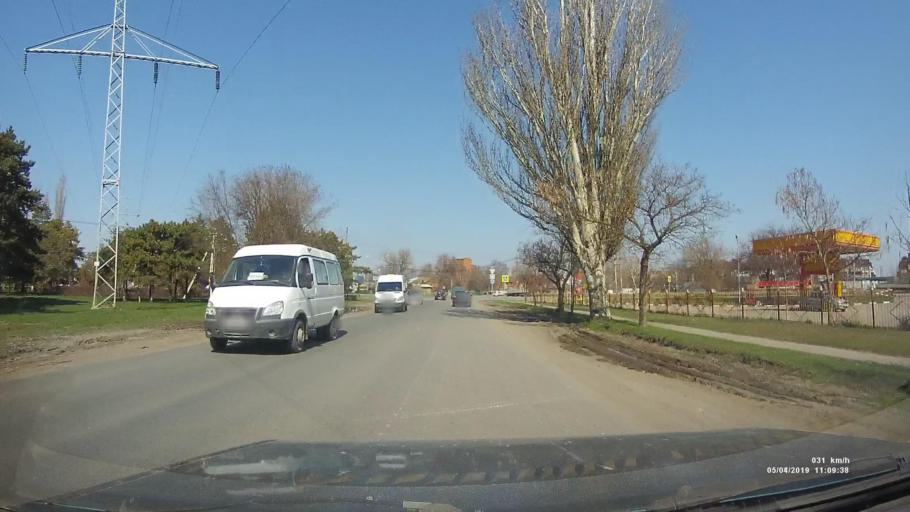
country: RU
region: Rostov
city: Azov
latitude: 47.0910
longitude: 39.4325
